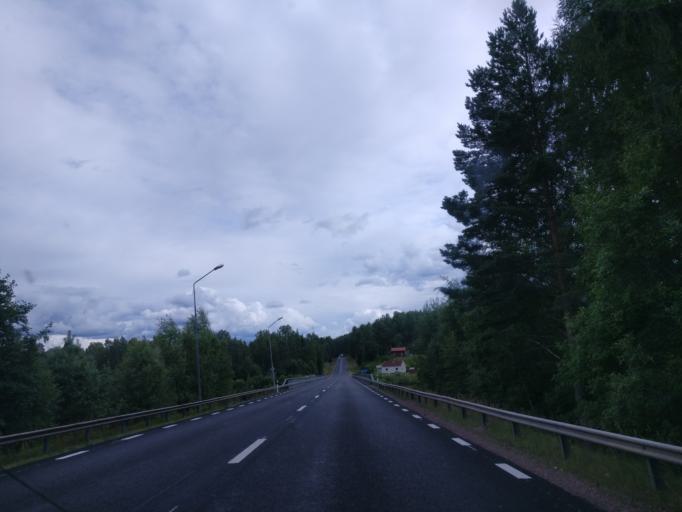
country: SE
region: Vaermland
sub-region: Hagfors Kommun
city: Ekshaerad
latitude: 60.0623
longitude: 13.5507
